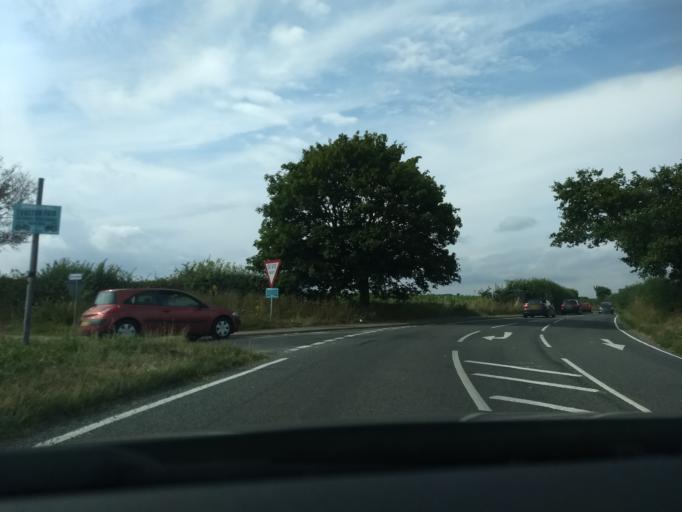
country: GB
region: England
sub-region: Suffolk
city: Ipswich
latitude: 52.0062
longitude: 1.1657
